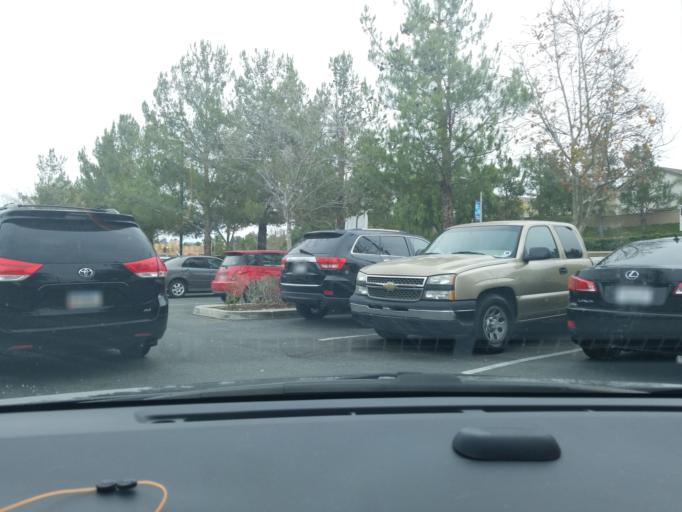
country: US
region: California
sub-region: Riverside County
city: Temecula
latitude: 33.5268
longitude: -117.1493
